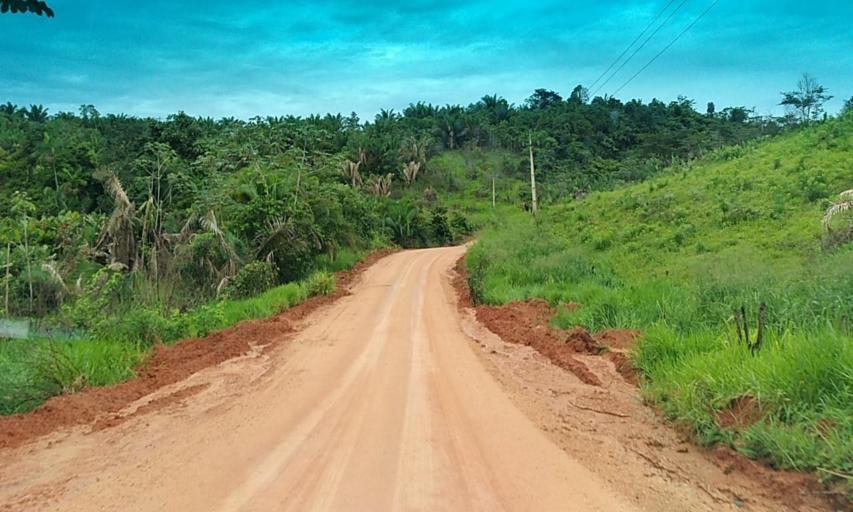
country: BR
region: Para
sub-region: Senador Jose Porfirio
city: Senador Jose Porfirio
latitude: -3.0780
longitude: -51.6348
